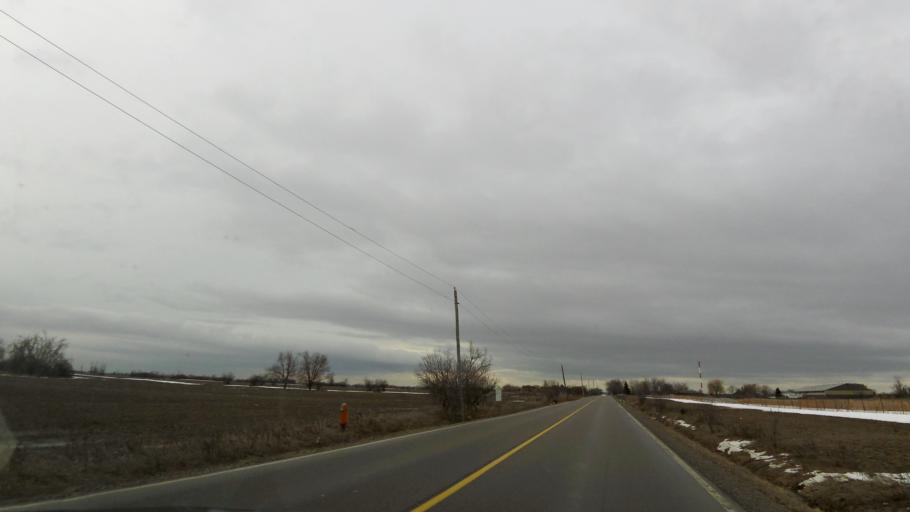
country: CA
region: Ontario
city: Brampton
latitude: 43.8295
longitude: -79.6966
